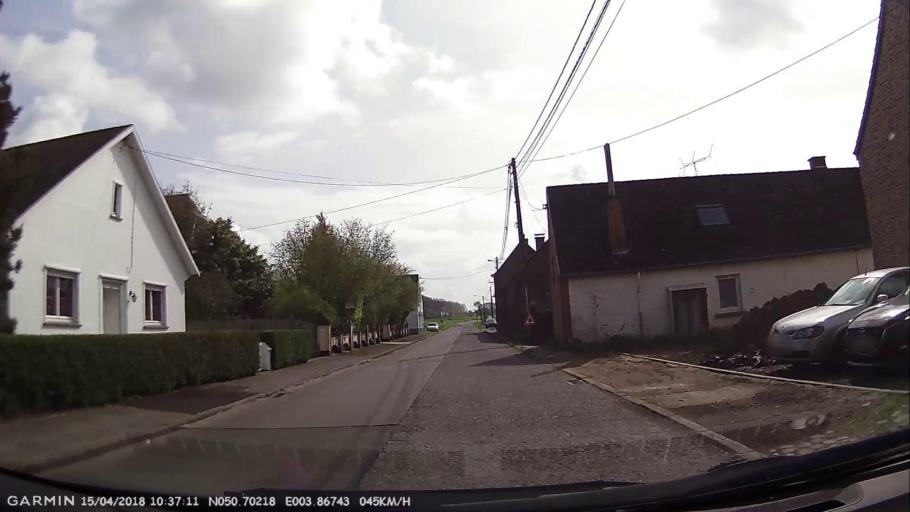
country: BE
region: Wallonia
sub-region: Province du Hainaut
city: Lessines
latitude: 50.7022
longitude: 3.8676
